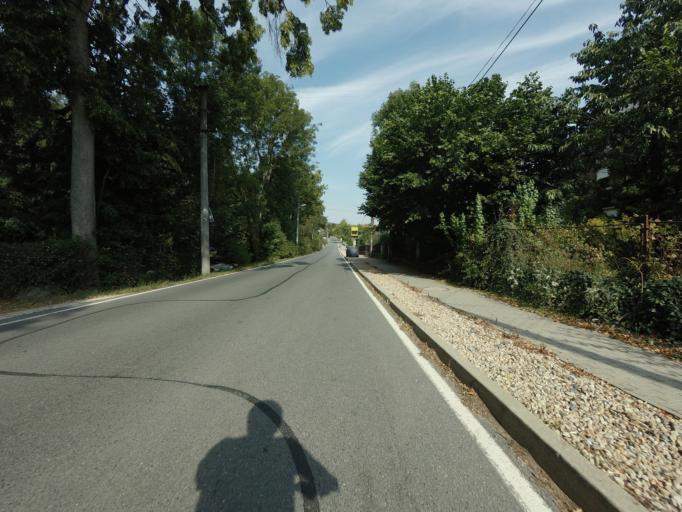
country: CZ
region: Central Bohemia
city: Petrovice
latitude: 49.5507
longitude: 14.3432
